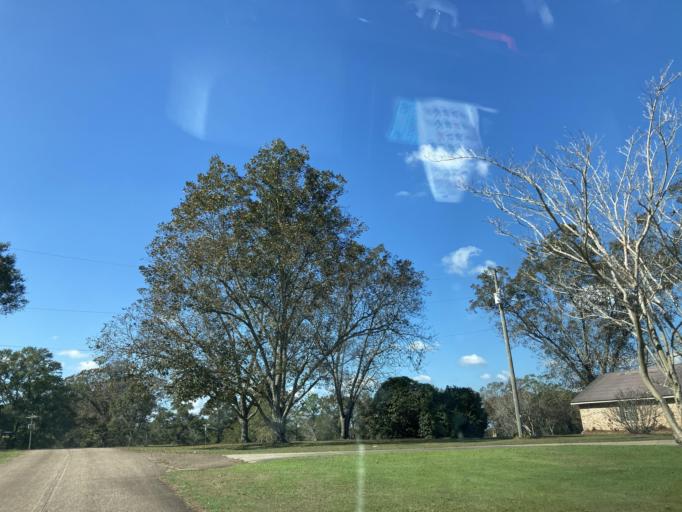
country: US
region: Mississippi
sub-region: Lamar County
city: Sumrall
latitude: 31.2989
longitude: -89.5381
